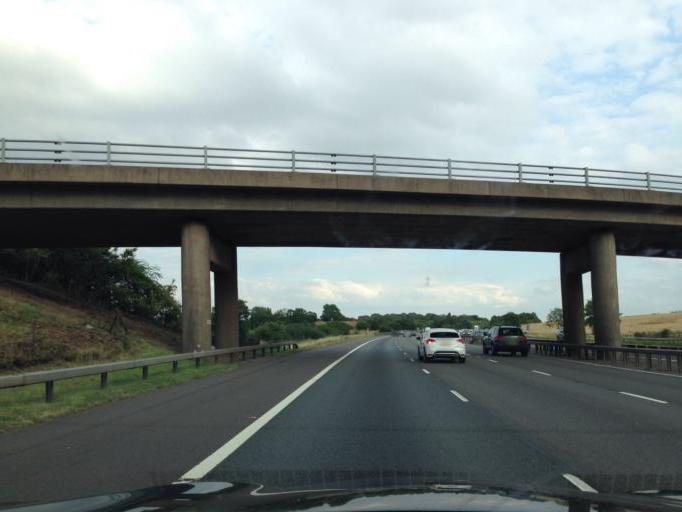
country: GB
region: England
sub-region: Warwickshire
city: Harbury
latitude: 52.2157
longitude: -1.4969
